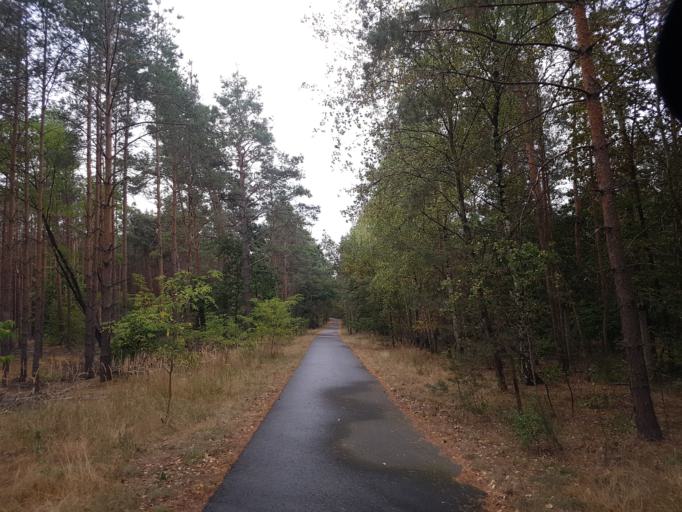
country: DE
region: Brandenburg
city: Finsterwalde
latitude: 51.6036
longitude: 13.7604
